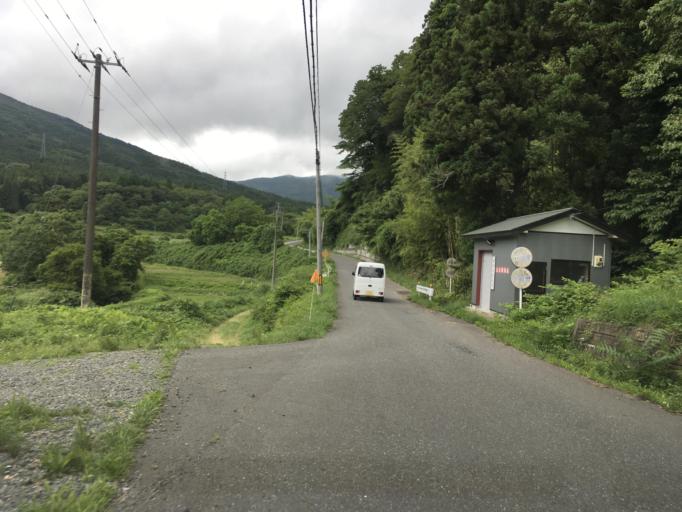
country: JP
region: Iwate
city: Ofunato
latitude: 38.8919
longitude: 141.4833
